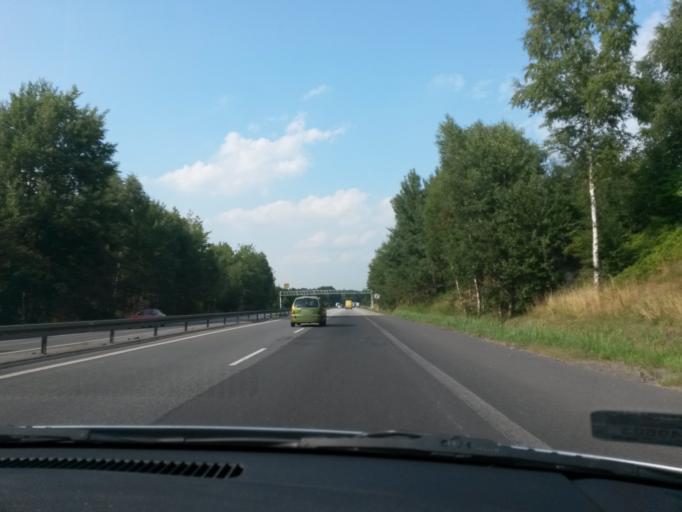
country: PL
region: Silesian Voivodeship
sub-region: Dabrowa Gornicza
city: Dabrowa Gornicza
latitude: 50.2884
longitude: 19.2175
